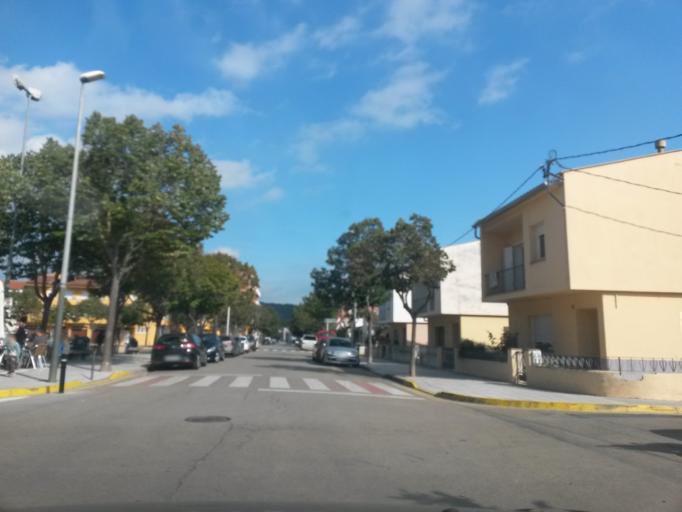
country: ES
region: Catalonia
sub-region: Provincia de Girona
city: Bescano
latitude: 41.9636
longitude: 2.7382
